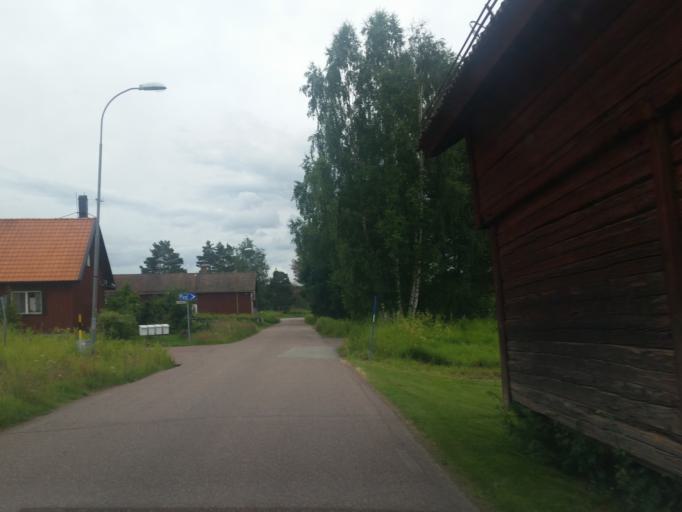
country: SE
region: Dalarna
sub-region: Leksand Municipality
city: Smedby
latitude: 60.6745
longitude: 15.0964
